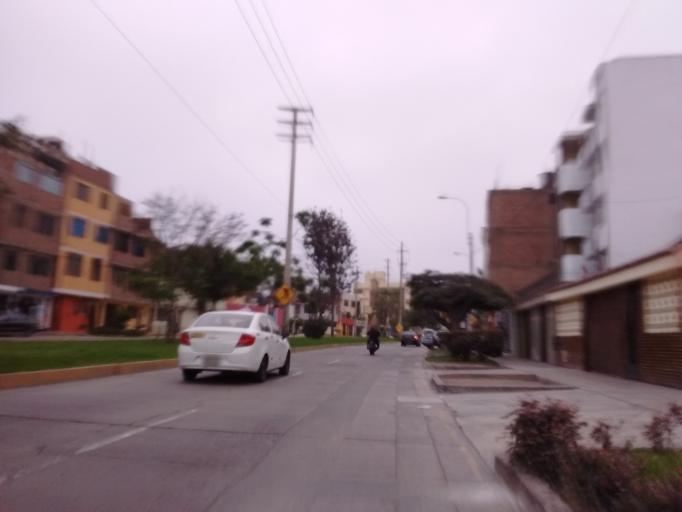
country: PE
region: Lima
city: Lima
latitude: -12.0627
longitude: -77.0696
